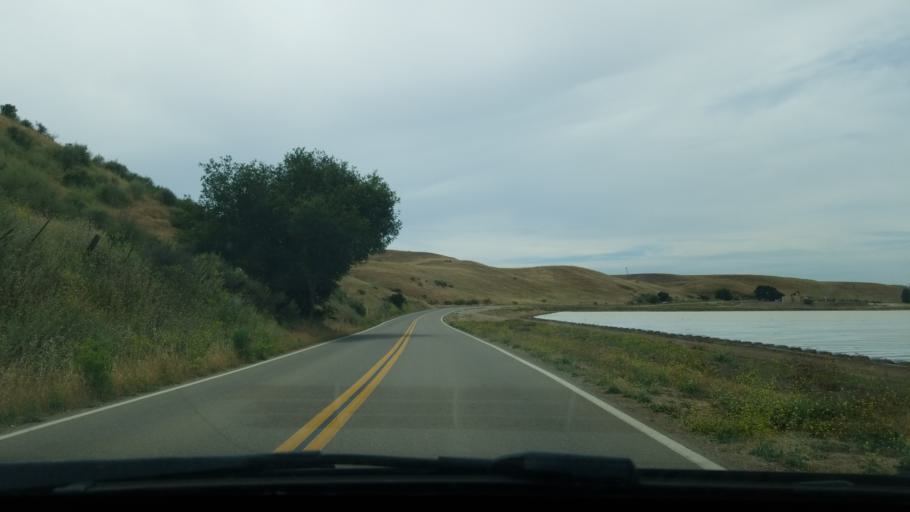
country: US
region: California
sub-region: Santa Barbara County
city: Orcutt
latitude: 34.8729
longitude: -120.3053
